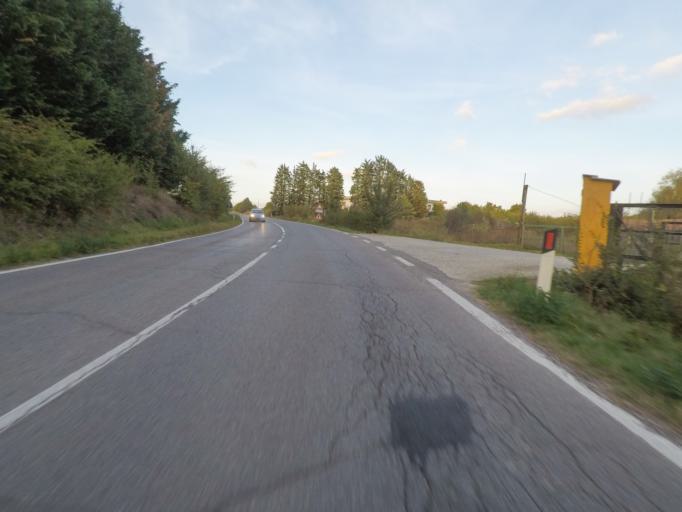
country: IT
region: Tuscany
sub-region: Provincia di Siena
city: Pienza
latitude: 43.0851
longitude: 11.6776
